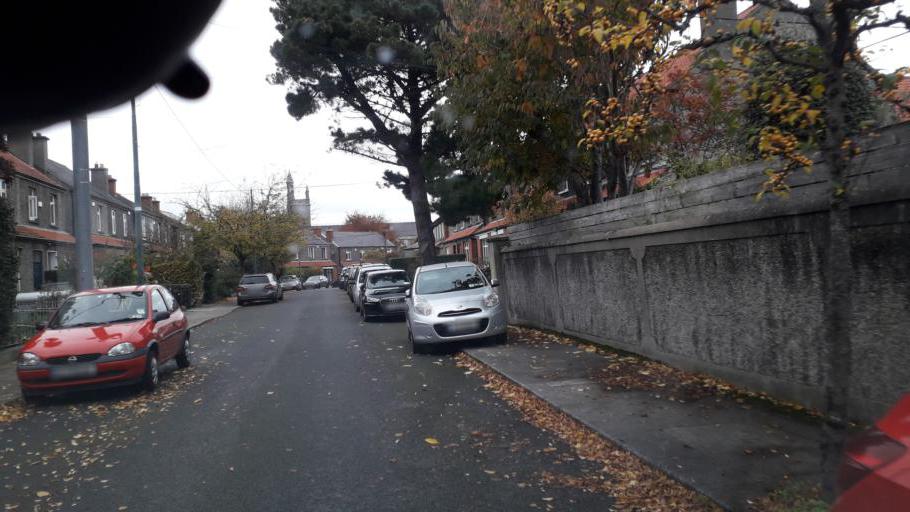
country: IE
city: Milltown
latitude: 53.3165
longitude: -6.2527
